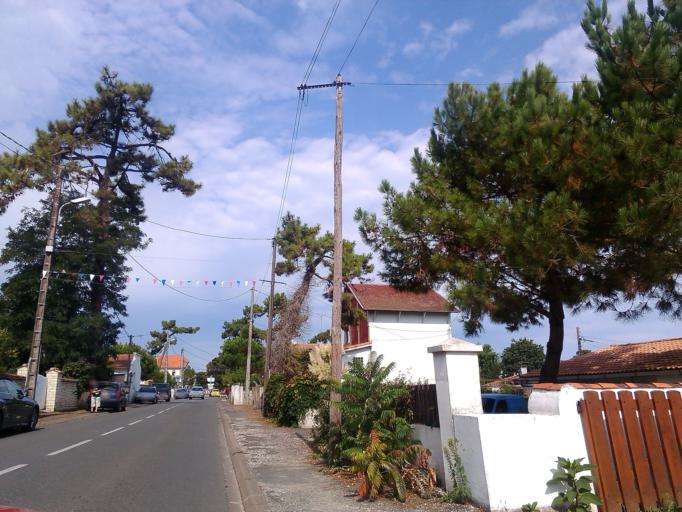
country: FR
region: Poitou-Charentes
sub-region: Departement de la Charente-Maritime
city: La Tremblade
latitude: 45.7950
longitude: -1.1655
